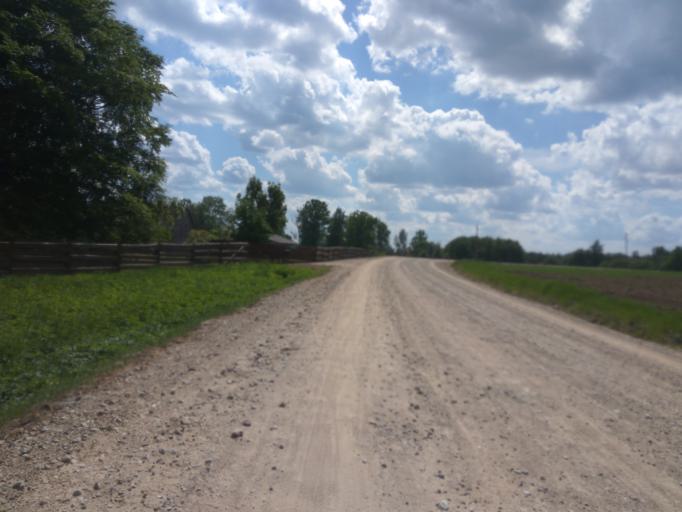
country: LV
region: Kuldigas Rajons
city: Kuldiga
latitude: 56.9053
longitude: 21.9650
